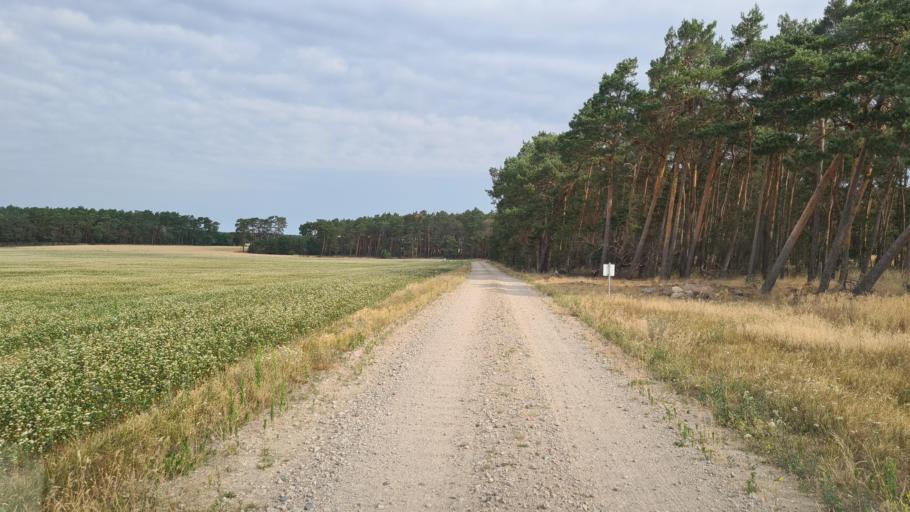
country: DE
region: Brandenburg
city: Linthe
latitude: 52.1018
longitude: 12.7901
